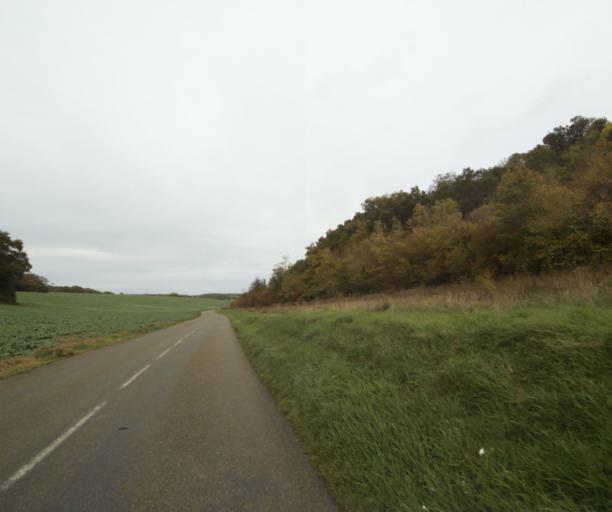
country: FR
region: Centre
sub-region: Departement d'Eure-et-Loir
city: Dreux
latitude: 48.7639
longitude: 1.3529
